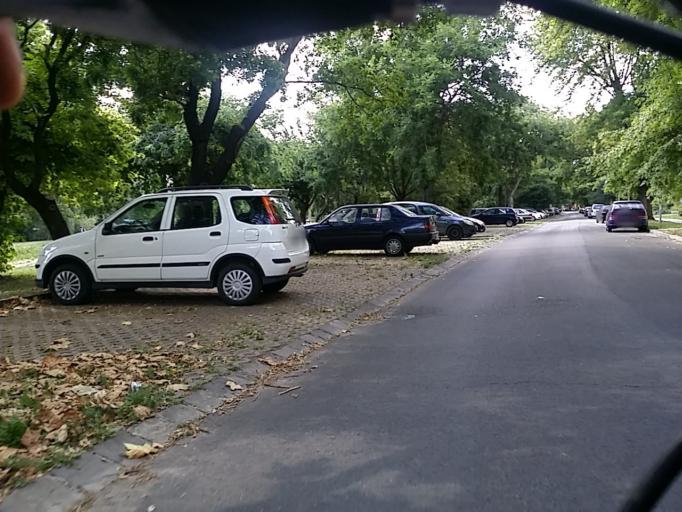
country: HU
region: Budapest
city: Budapest XIII. keruelet
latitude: 47.5398
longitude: 19.0830
